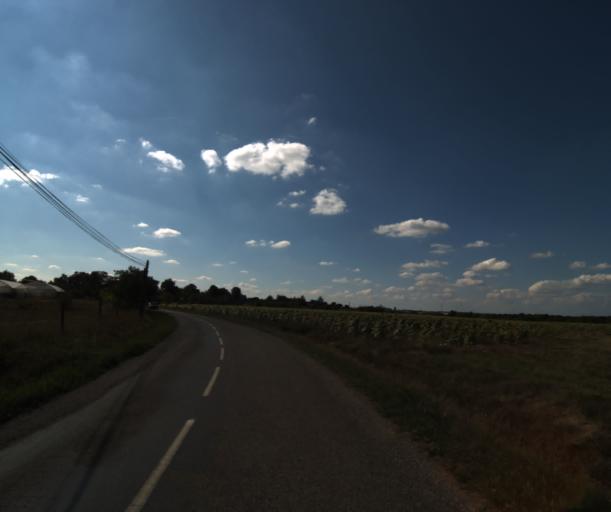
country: FR
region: Midi-Pyrenees
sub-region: Departement de la Haute-Garonne
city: Saint-Lys
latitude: 43.5038
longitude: 1.2041
